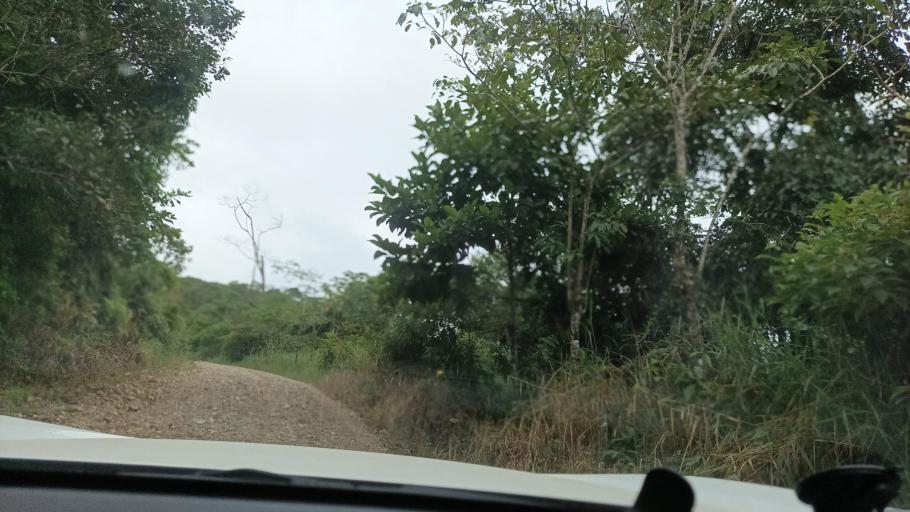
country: MX
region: Veracruz
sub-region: Uxpanapa
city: Poblado 10
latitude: 17.4390
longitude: -94.4129
